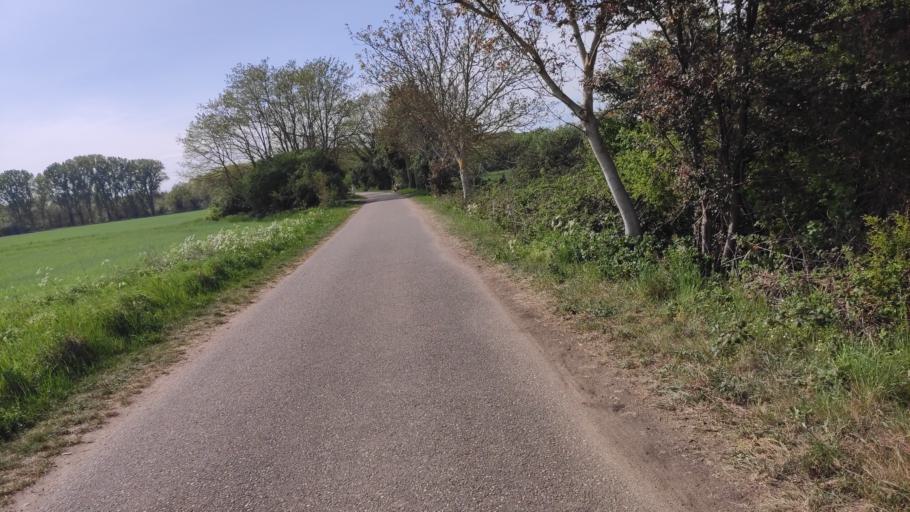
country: DE
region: Baden-Wuerttemberg
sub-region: Freiburg Region
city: Umkirch
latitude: 48.0100
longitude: 7.7737
